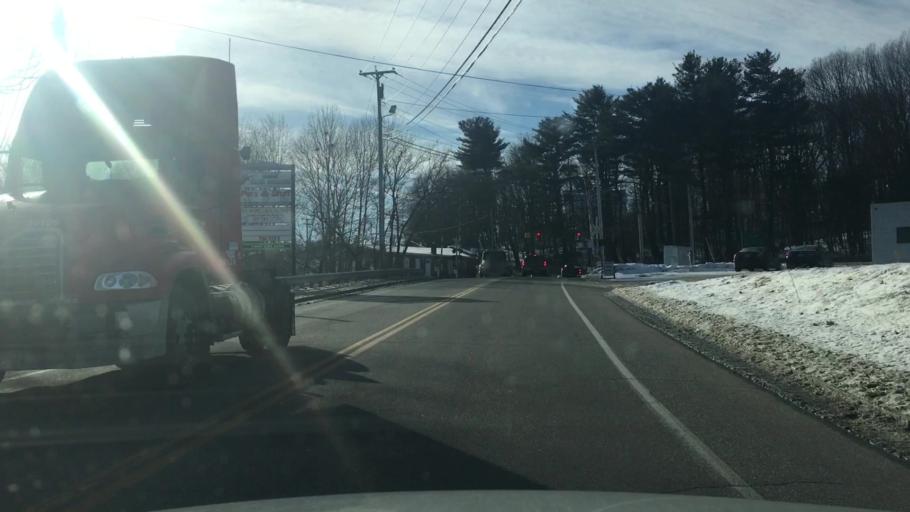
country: US
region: Maine
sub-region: Androscoggin County
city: Auburn
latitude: 44.0914
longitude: -70.2293
